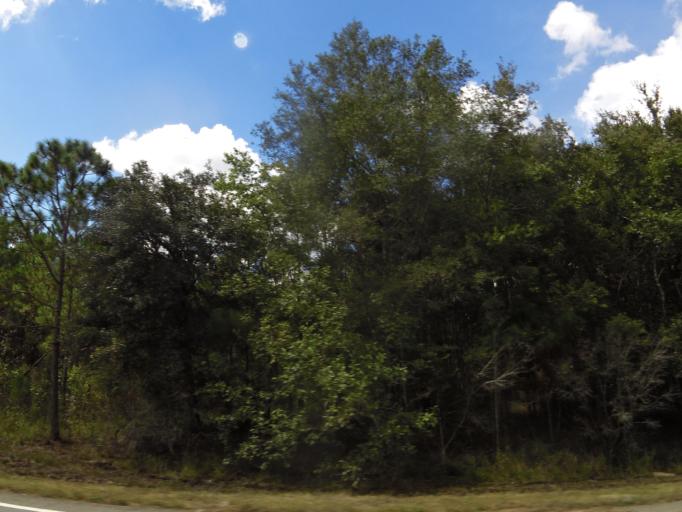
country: US
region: Georgia
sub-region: Charlton County
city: Folkston
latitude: 31.0097
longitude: -82.0265
